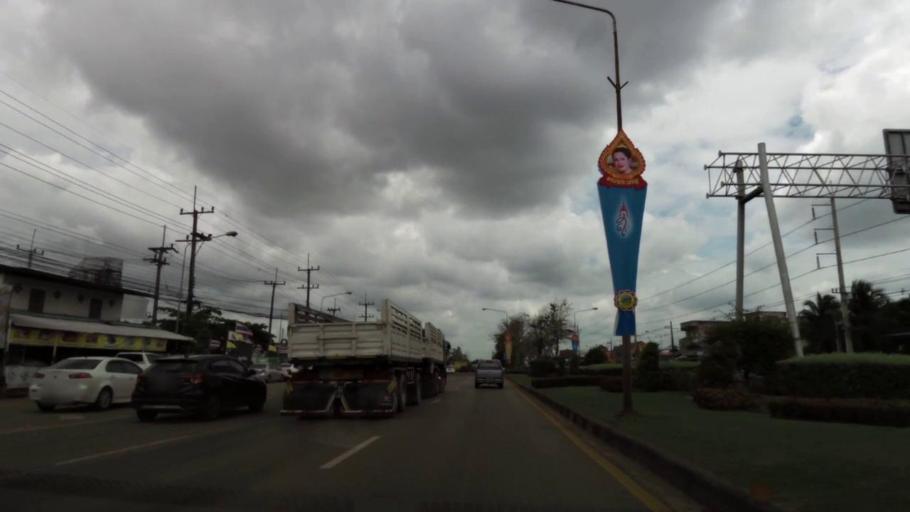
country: TH
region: Rayong
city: Klaeng
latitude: 12.7775
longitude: 101.7086
